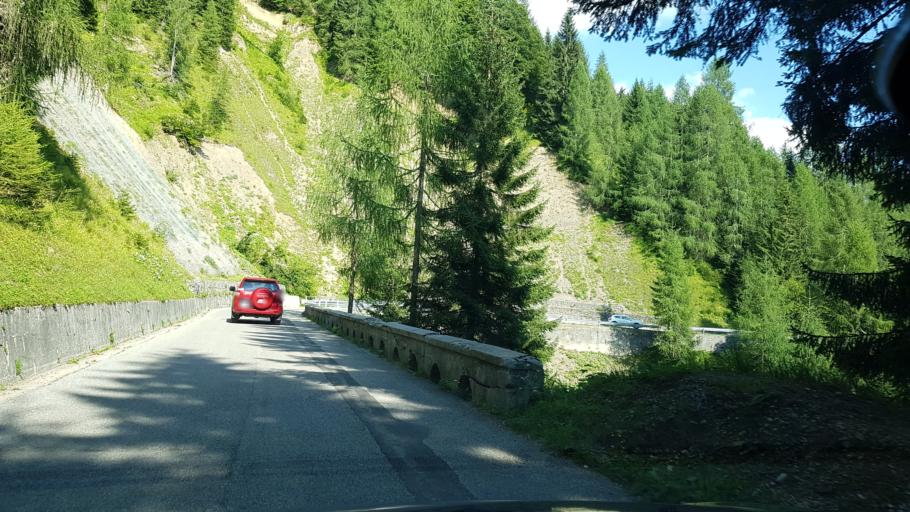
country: IT
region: Friuli Venezia Giulia
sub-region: Provincia di Udine
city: Sauris di Sotto
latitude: 46.4741
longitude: 12.6683
